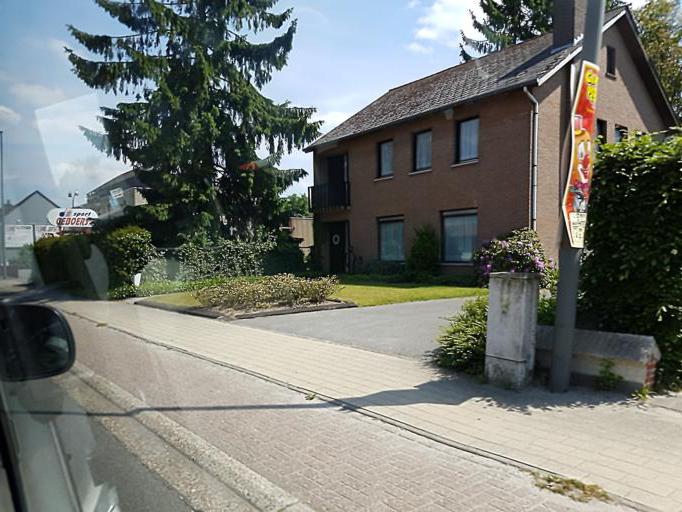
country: BE
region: Flanders
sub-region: Provincie Limburg
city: Lommel
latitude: 51.2306
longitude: 5.3270
